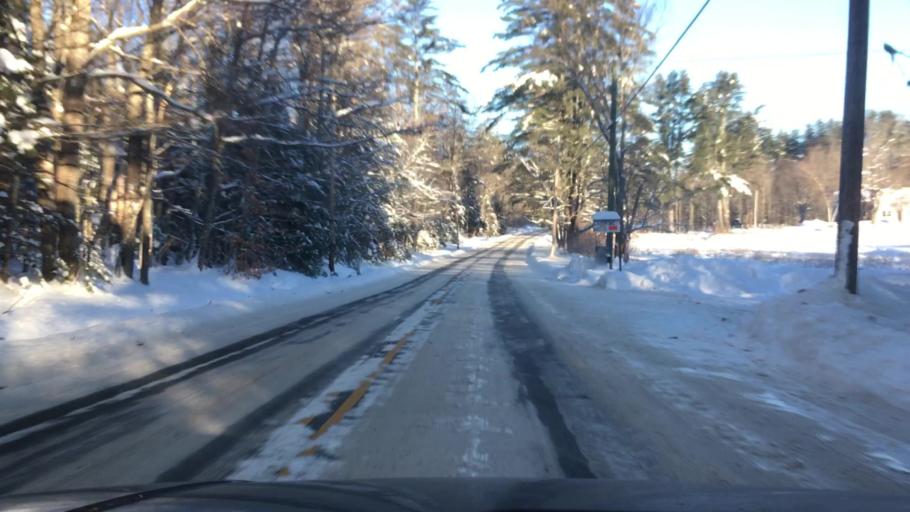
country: US
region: Maine
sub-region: Oxford County
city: Lovell
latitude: 44.1490
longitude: -70.9809
